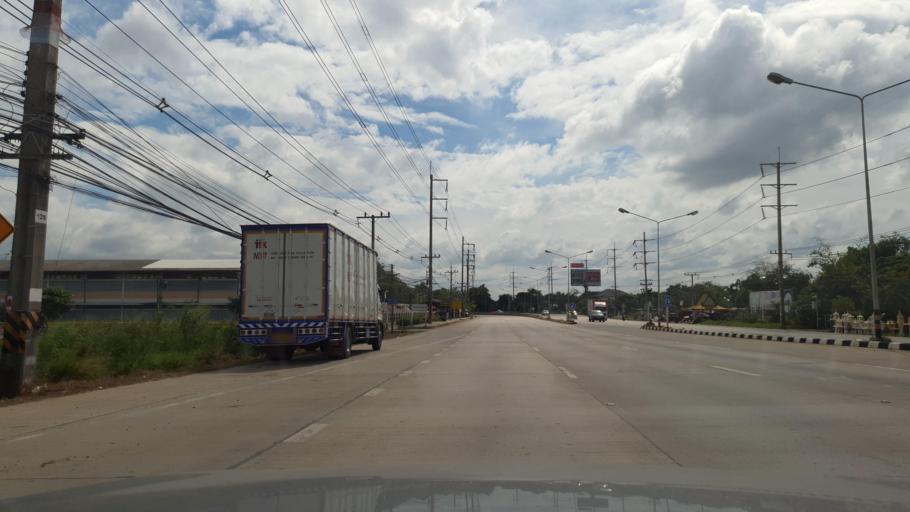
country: TH
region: Chachoengsao
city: Bang Pakong
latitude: 13.5422
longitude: 100.9895
